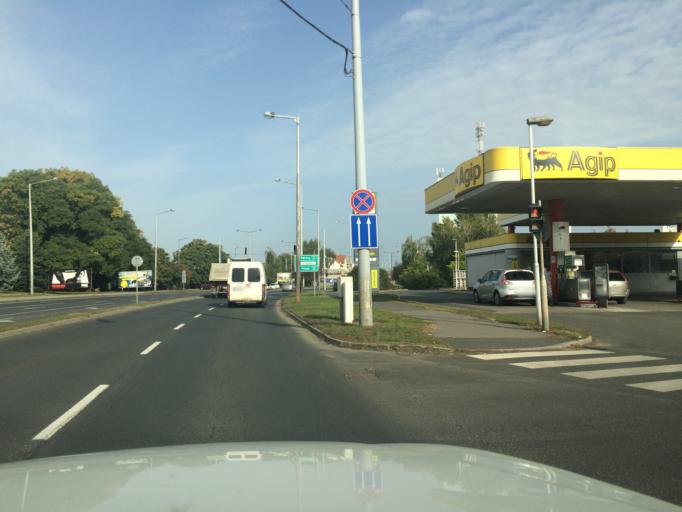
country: HU
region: Szabolcs-Szatmar-Bereg
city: Nyiregyhaza
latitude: 47.9539
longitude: 21.7042
